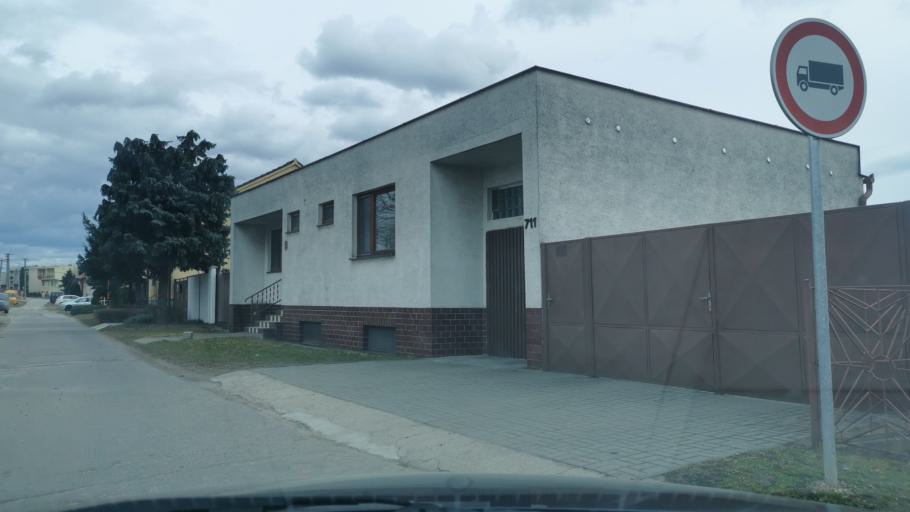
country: CZ
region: South Moravian
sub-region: Okres Breclav
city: Lanzhot
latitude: 48.6881
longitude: 17.0060
